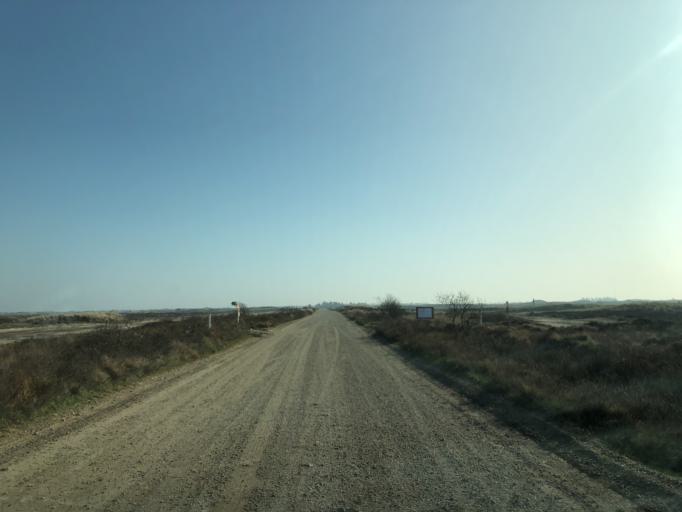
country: DK
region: South Denmark
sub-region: Varde Kommune
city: Oksbol
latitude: 55.5787
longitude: 8.1424
